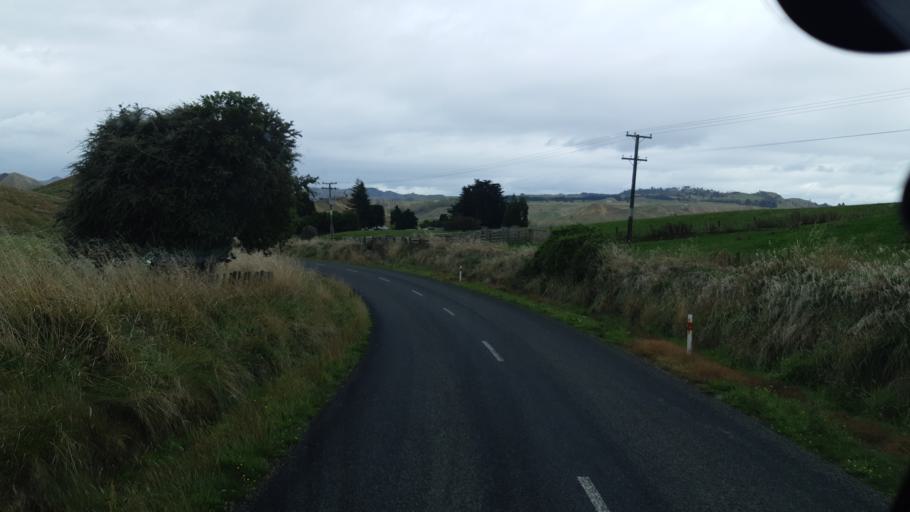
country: NZ
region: Manawatu-Wanganui
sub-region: Ruapehu District
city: Waiouru
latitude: -39.5537
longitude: 175.6052
